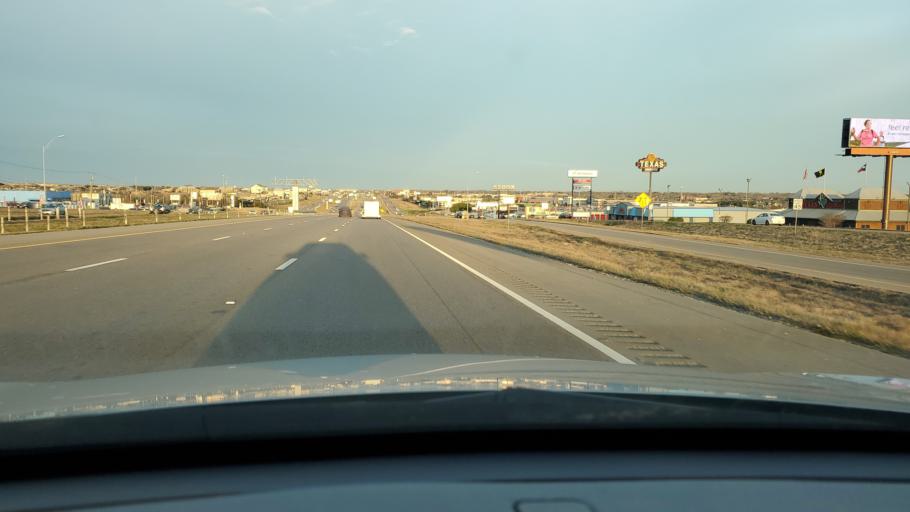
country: US
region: Texas
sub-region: Bell County
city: Harker Heights
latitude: 31.0816
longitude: -97.7006
